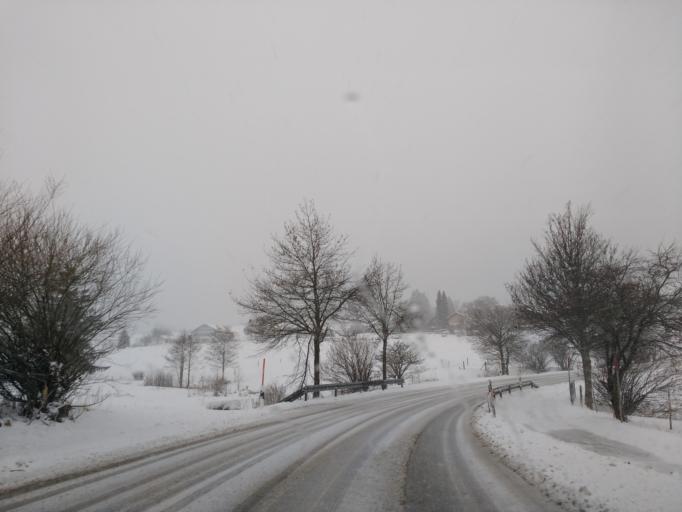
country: DE
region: Bavaria
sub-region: Swabia
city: Buchenberg
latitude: 47.7045
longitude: 10.2053
